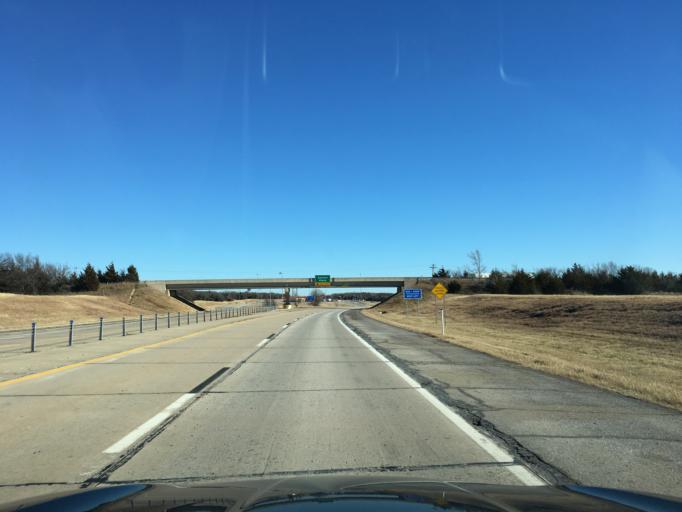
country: US
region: Oklahoma
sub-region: Pawnee County
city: Pawnee
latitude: 36.2247
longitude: -96.8042
